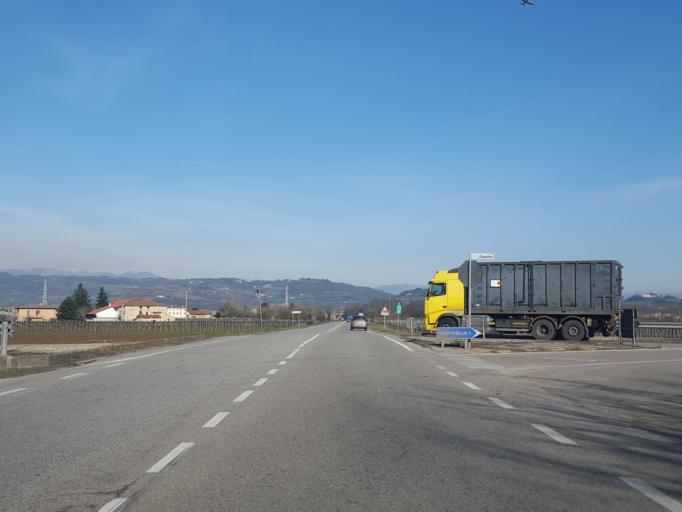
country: IT
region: Veneto
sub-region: Provincia di Vicenza
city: Monticello di Fara
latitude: 45.4220
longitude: 11.3765
